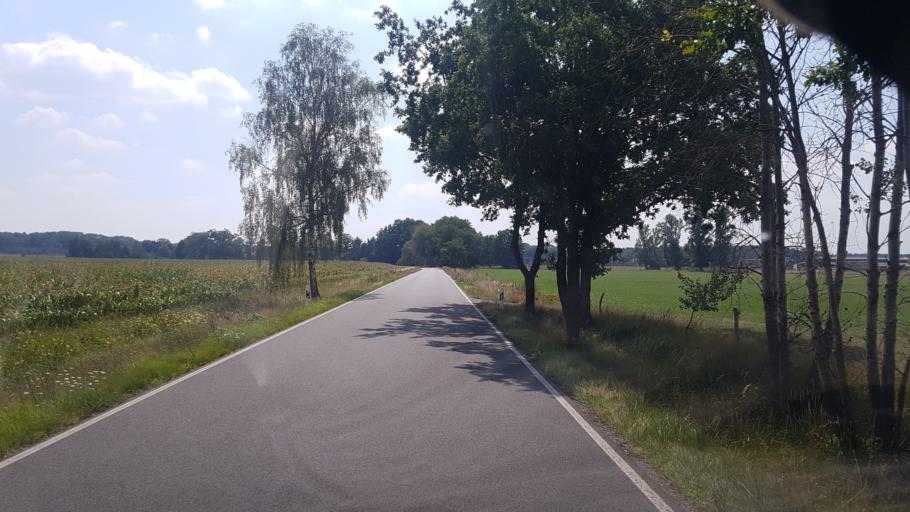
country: DE
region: Brandenburg
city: Cottbus
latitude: 51.7034
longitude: 14.4262
